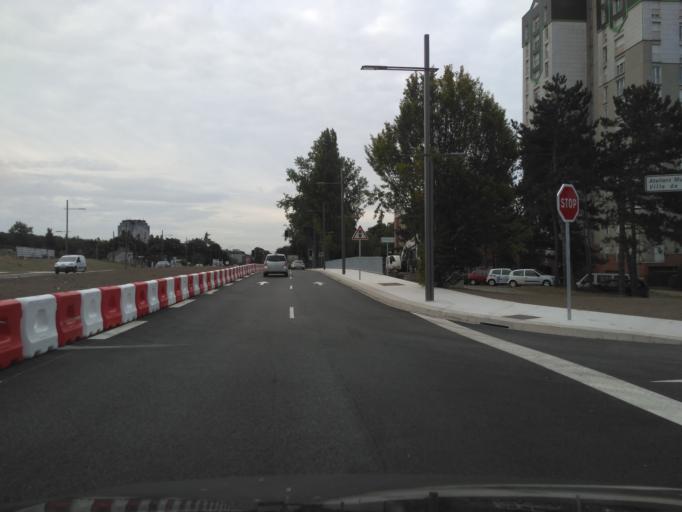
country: FR
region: Ile-de-France
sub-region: Departement de Seine-et-Marne
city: Vert-Saint-Denis
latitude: 48.5561
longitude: 2.6394
